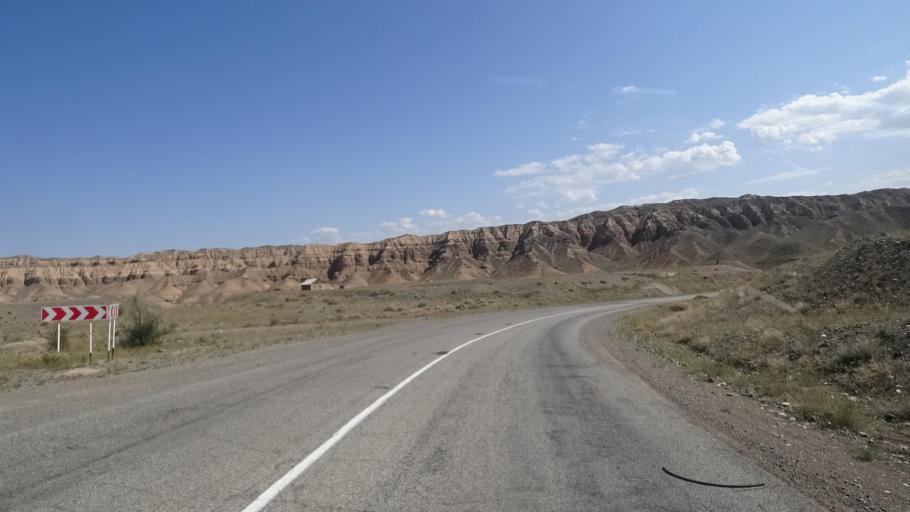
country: KZ
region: Almaty Oblysy
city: Kegen
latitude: 43.2721
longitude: 78.9708
